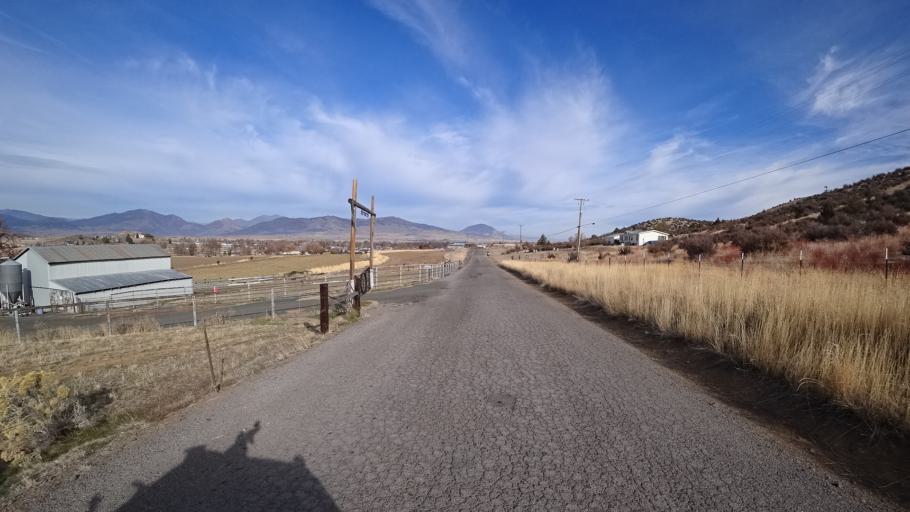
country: US
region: California
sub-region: Siskiyou County
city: Montague
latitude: 41.7158
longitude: -122.5215
